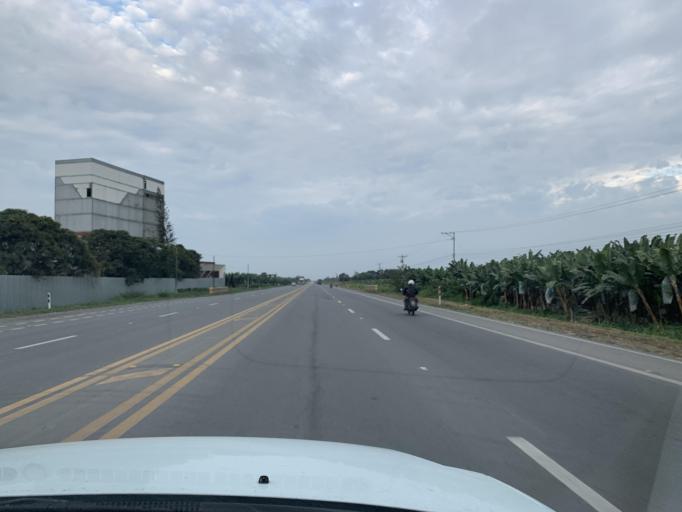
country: EC
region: Guayas
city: Naranjito
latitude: -2.2548
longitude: -79.6164
